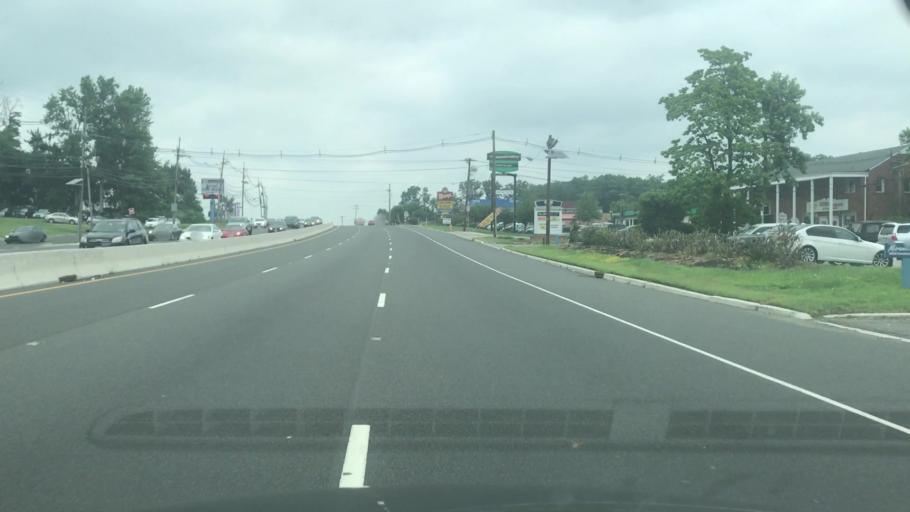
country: US
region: New Jersey
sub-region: Passaic County
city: Wayne
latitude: 40.9355
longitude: -74.2691
